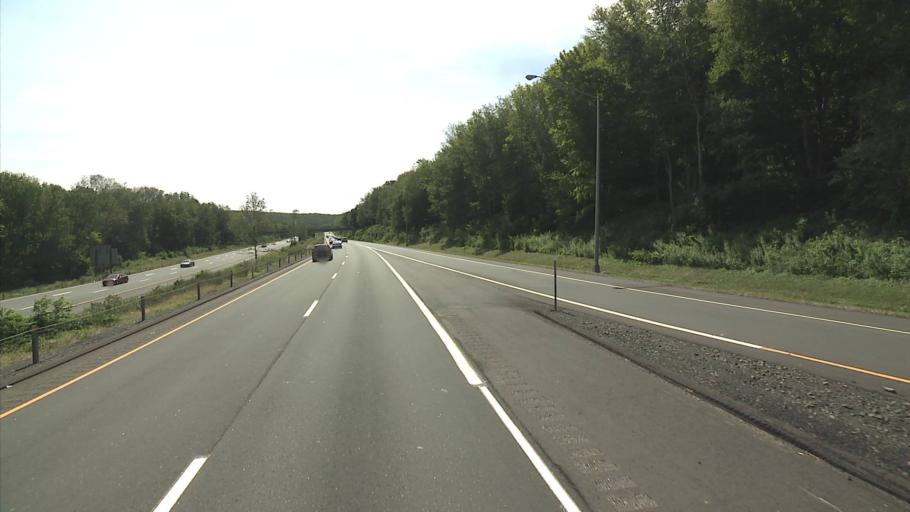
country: US
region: Connecticut
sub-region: Hartford County
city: Terramuggus
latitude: 41.6322
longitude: -72.4555
